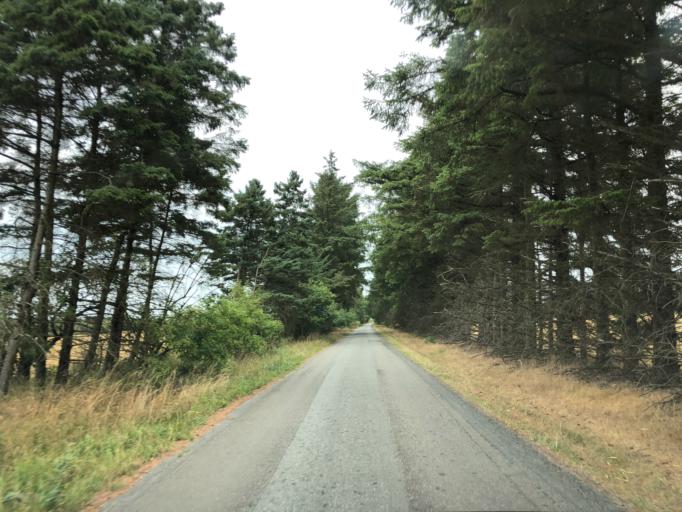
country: DK
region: Central Jutland
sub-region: Holstebro Kommune
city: Ulfborg
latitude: 56.2156
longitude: 8.3193
